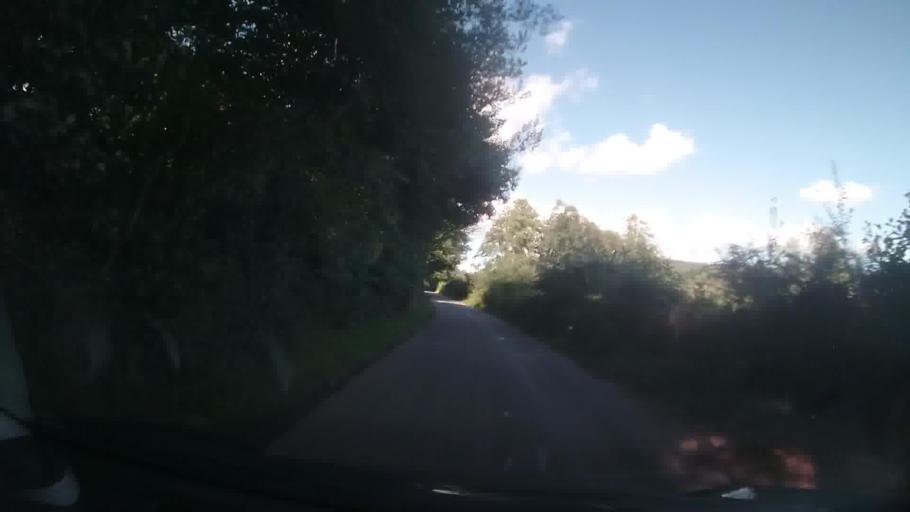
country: GB
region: Wales
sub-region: Sir Powys
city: Brecon
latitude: 51.8721
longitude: -3.3081
